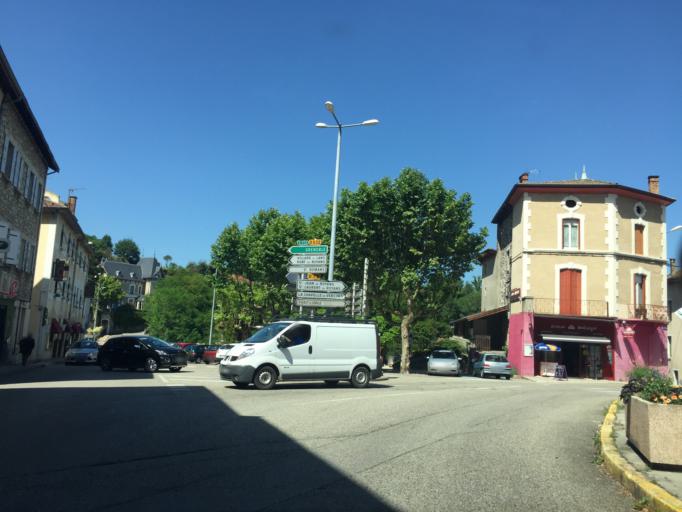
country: FR
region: Rhone-Alpes
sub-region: Departement de l'Isere
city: Saint-Hilaire-du-Rosier
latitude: 45.0605
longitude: 5.2470
